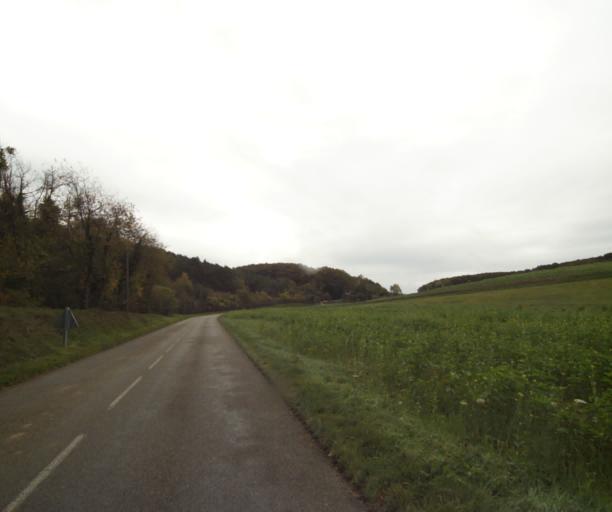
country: FR
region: Centre
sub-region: Departement d'Eure-et-Loir
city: Dreux
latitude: 48.7703
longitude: 1.3507
